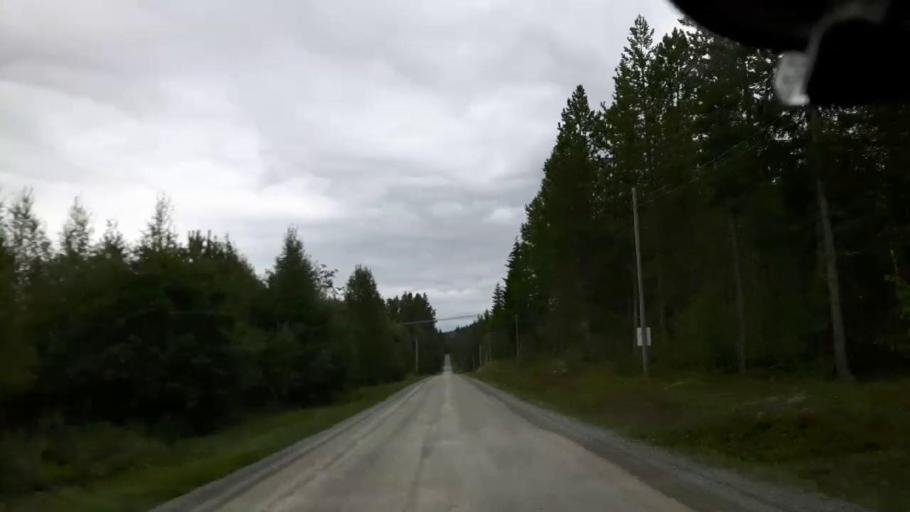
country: SE
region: Jaemtland
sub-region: Braecke Kommun
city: Braecke
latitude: 63.0939
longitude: 15.2491
